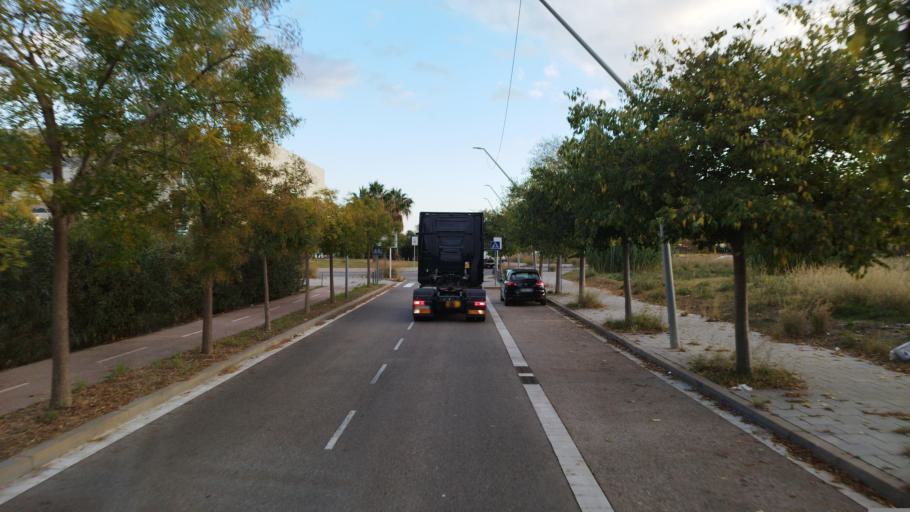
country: ES
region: Catalonia
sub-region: Provincia de Barcelona
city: Viladecans
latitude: 41.3023
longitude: 2.0174
